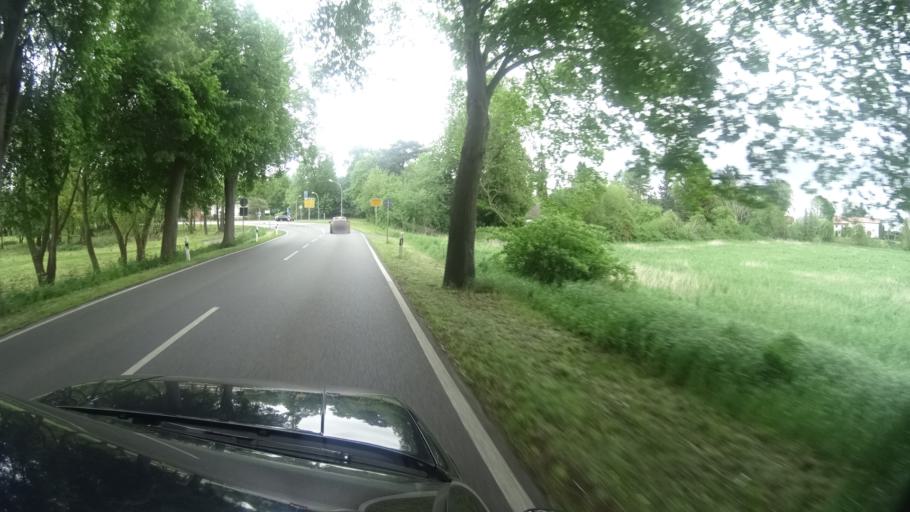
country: DE
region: Brandenburg
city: Fehrbellin
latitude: 52.8363
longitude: 12.7802
